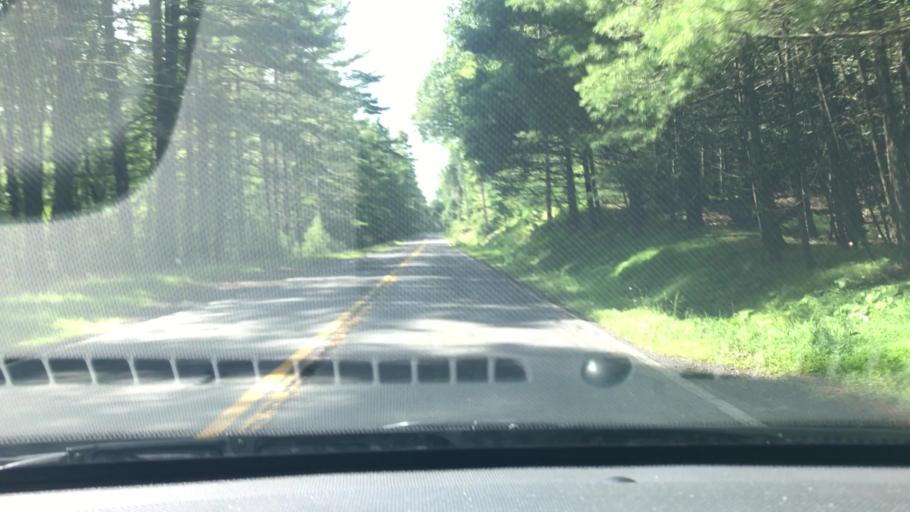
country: US
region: New York
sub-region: Ulster County
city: Shokan
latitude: 41.9436
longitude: -74.2427
